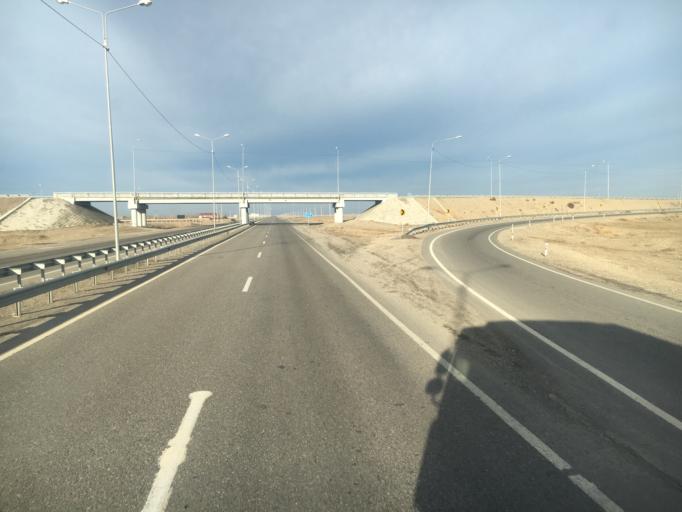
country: KZ
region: Ongtustik Qazaqstan
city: Turkestan
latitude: 43.4140
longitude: 68.0269
